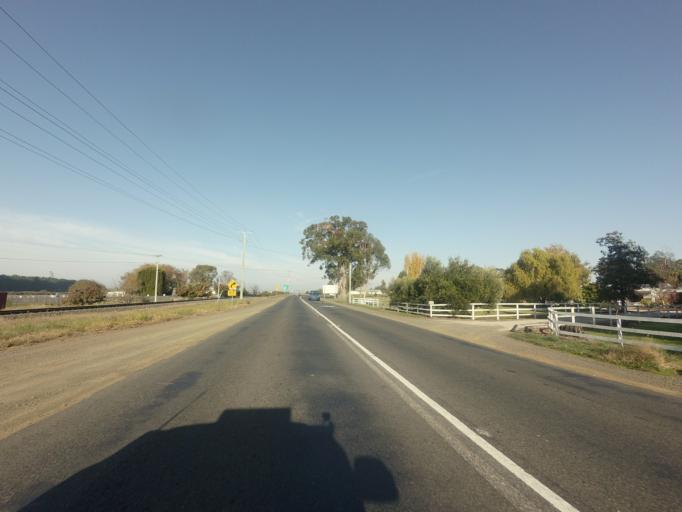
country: AU
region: Tasmania
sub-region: Northern Midlands
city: Perth
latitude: -41.5772
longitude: 147.1606
